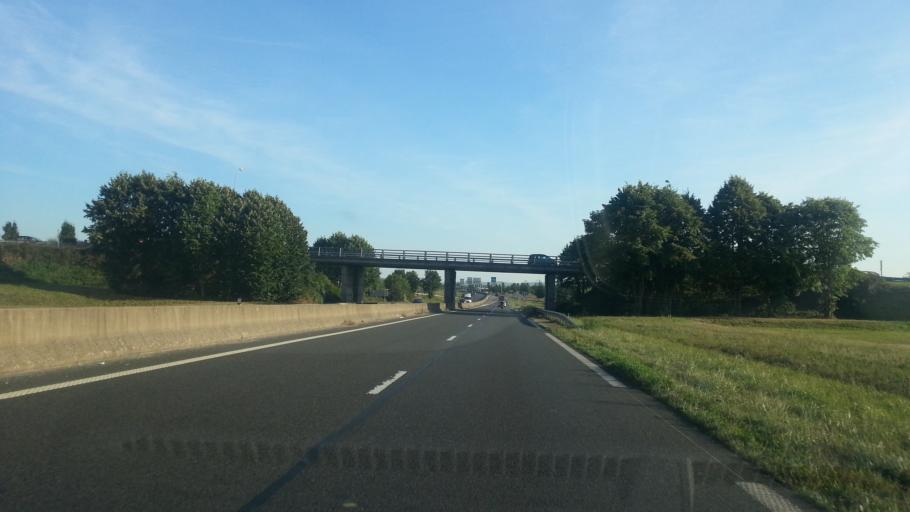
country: FR
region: Picardie
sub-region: Departement de l'Oise
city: Tille
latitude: 49.4393
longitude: 2.1136
